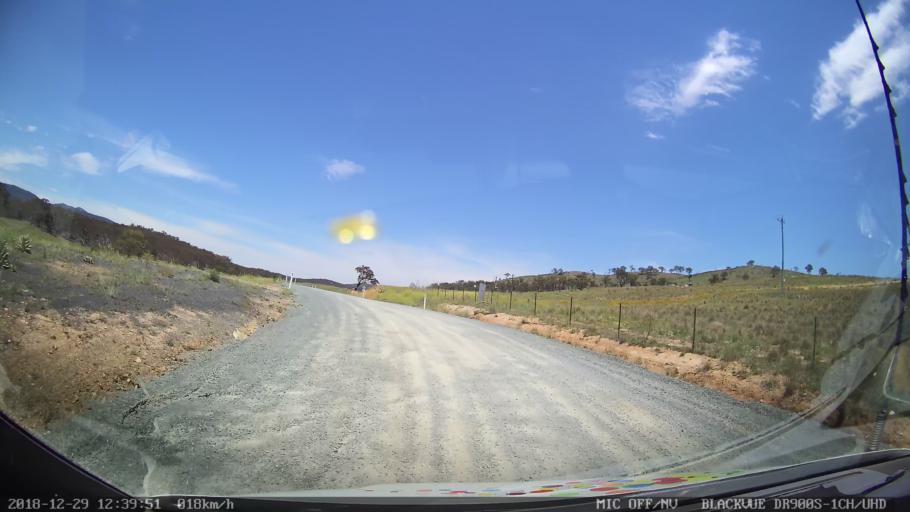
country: AU
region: Australian Capital Territory
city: Macarthur
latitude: -35.5979
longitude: 149.2266
